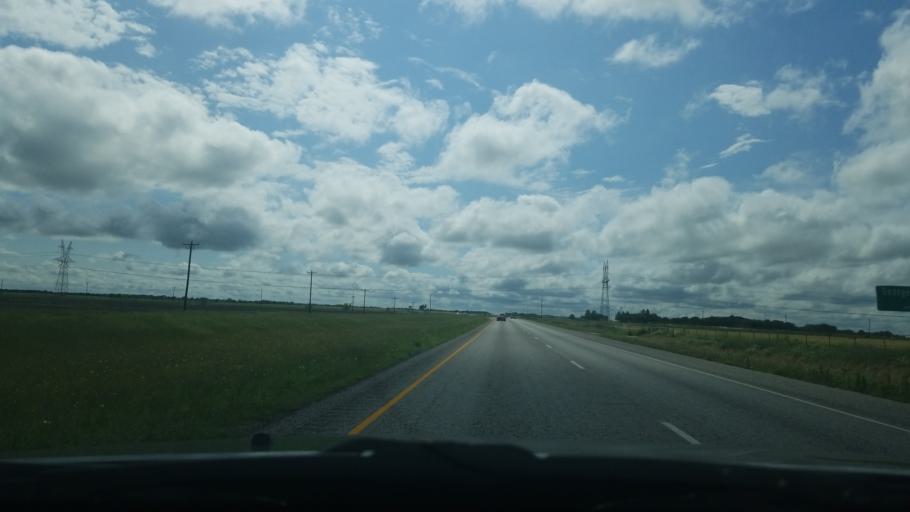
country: US
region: Texas
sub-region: Denton County
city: Ponder
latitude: 33.2370
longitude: -97.2884
